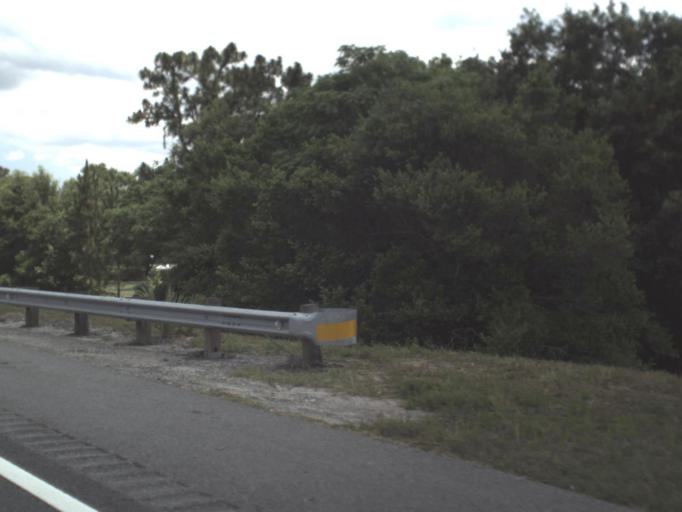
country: US
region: Florida
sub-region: Duval County
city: Jacksonville
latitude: 30.3320
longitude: -81.5331
